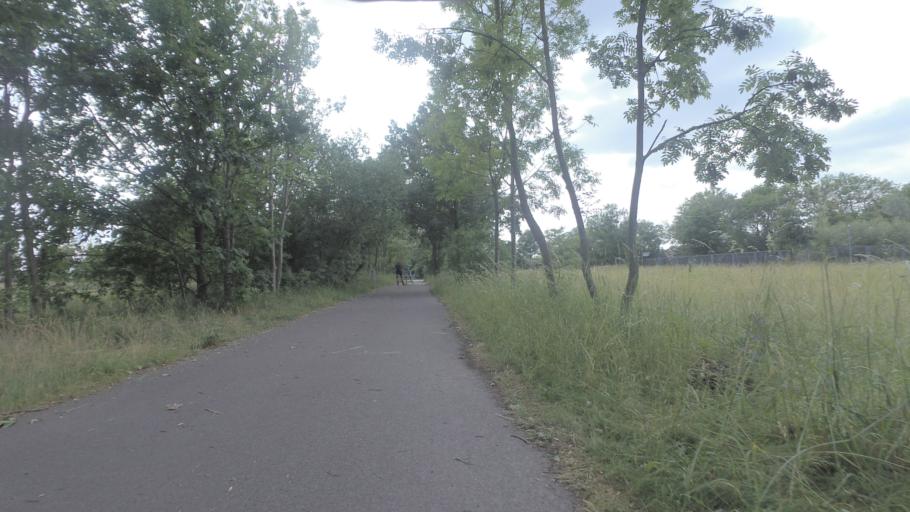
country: DE
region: Brandenburg
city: Schonefeld
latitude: 52.3996
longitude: 13.5019
